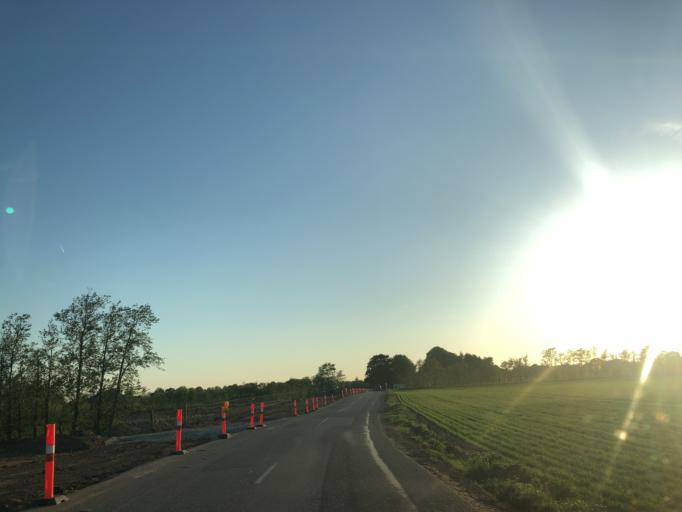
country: DK
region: Zealand
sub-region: Ringsted Kommune
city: Ringsted
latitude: 55.4075
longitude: 11.8717
